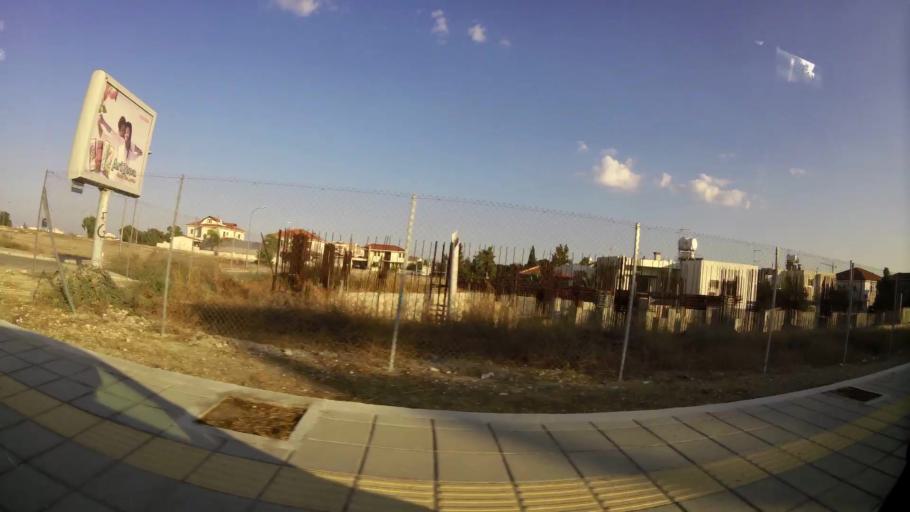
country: CY
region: Larnaka
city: Larnaca
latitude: 34.9272
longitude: 33.6031
